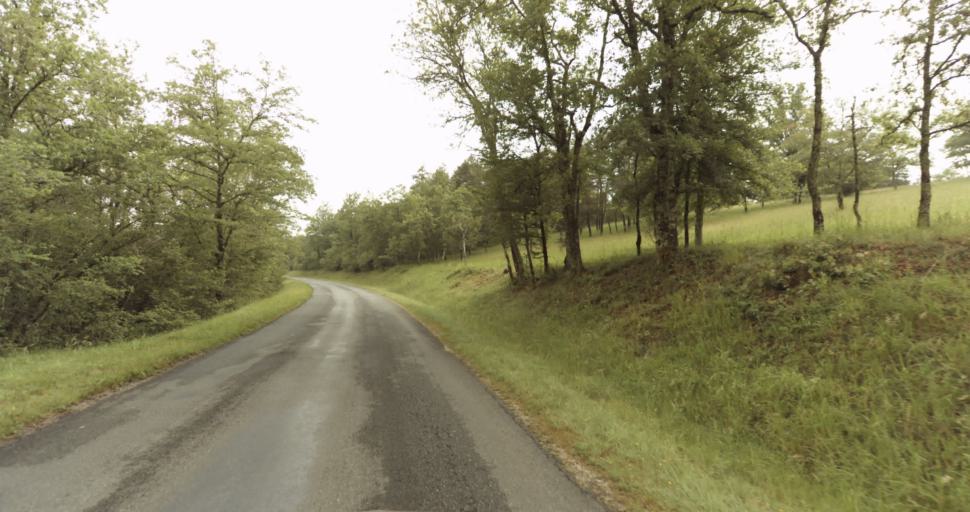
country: FR
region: Aquitaine
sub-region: Departement de la Dordogne
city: Lalinde
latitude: 44.8895
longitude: 0.7726
